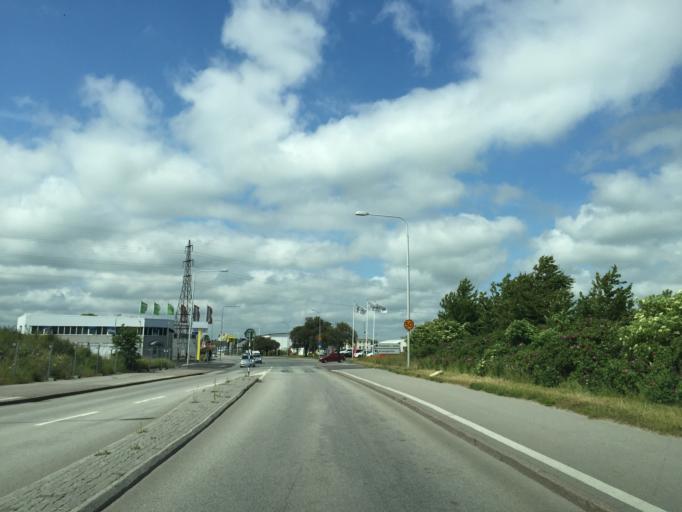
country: SE
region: Skane
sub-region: Ystads Kommun
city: Ystad
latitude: 55.4347
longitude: 13.8384
